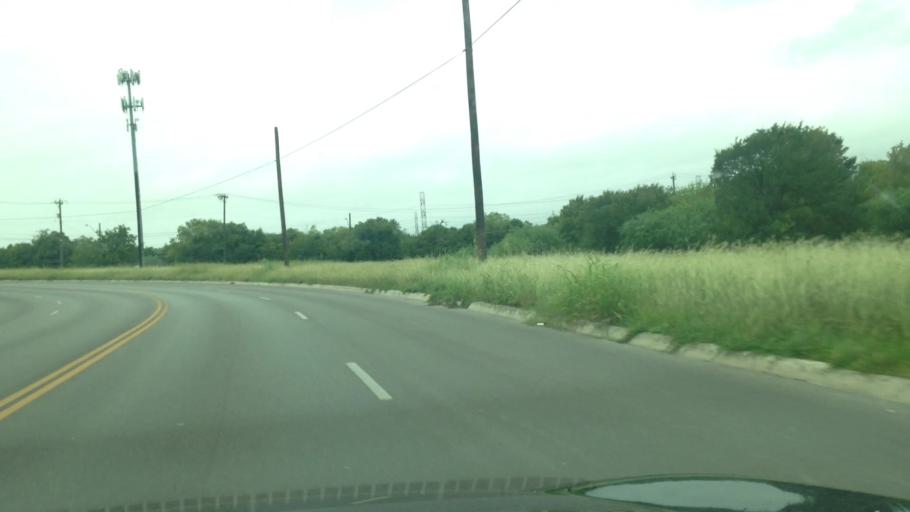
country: US
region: Texas
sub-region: Bexar County
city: Live Oak
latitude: 29.5799
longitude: -98.4006
